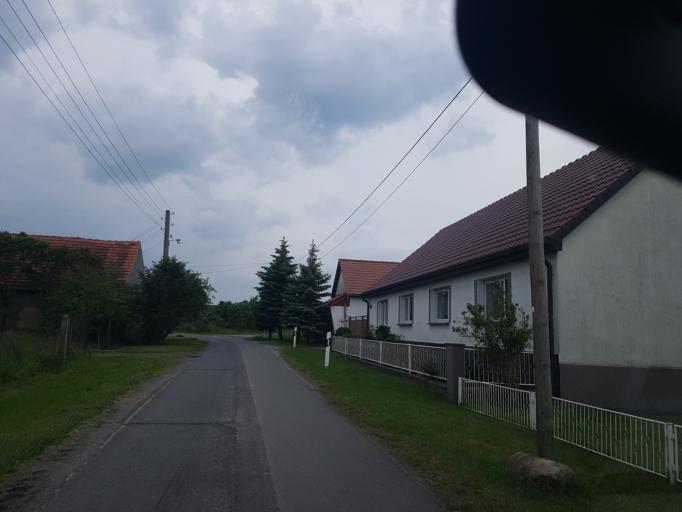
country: DE
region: Brandenburg
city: Finsterwalde
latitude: 51.5653
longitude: 13.6655
